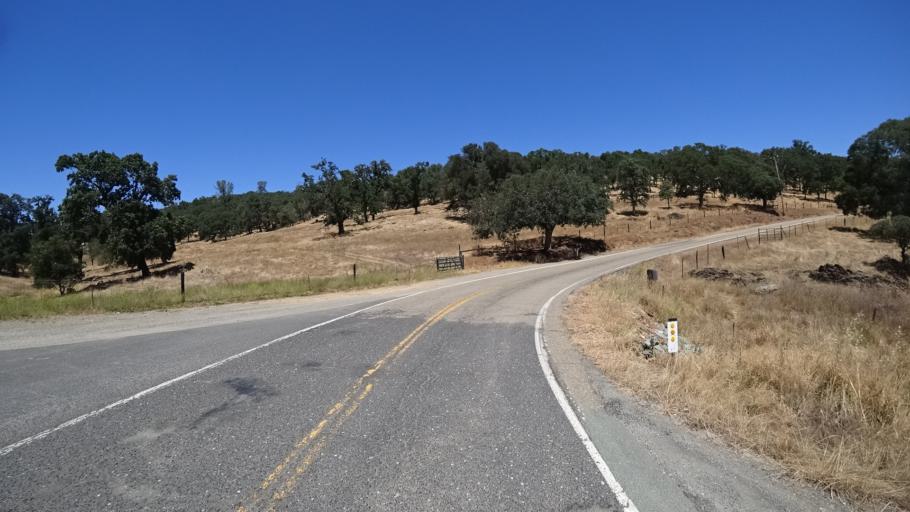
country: US
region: California
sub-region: Calaveras County
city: San Andreas
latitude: 38.0925
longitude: -120.6643
